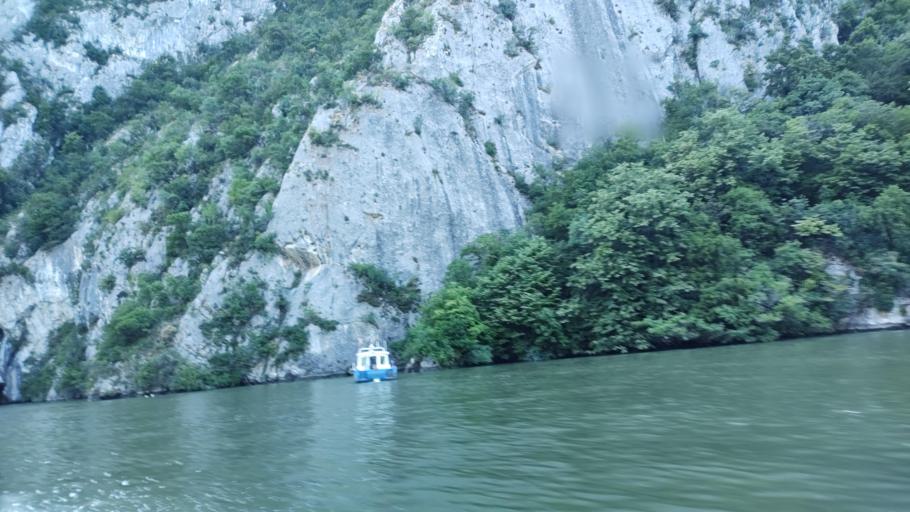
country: RO
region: Mehedinti
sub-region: Comuna Dubova
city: Dubova
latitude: 44.5963
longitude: 22.2627
